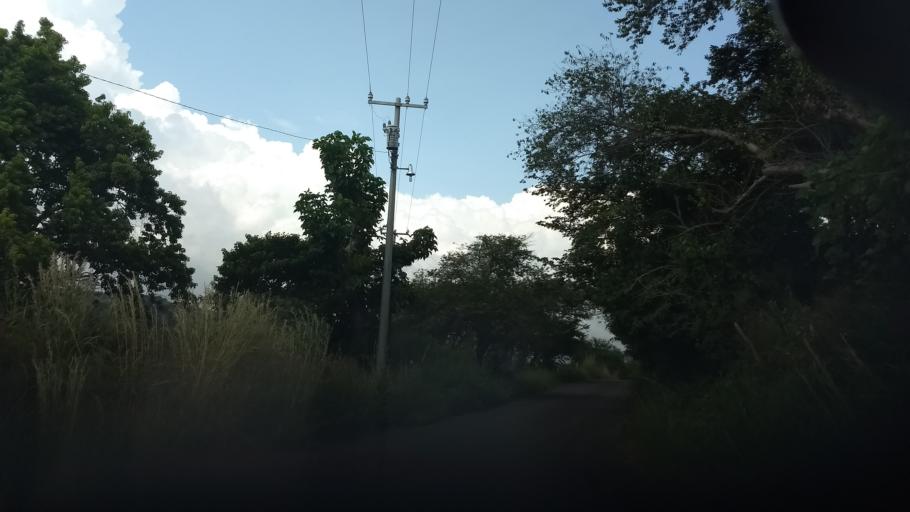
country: MX
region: Jalisco
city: Tonila
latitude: 19.4105
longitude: -103.4866
